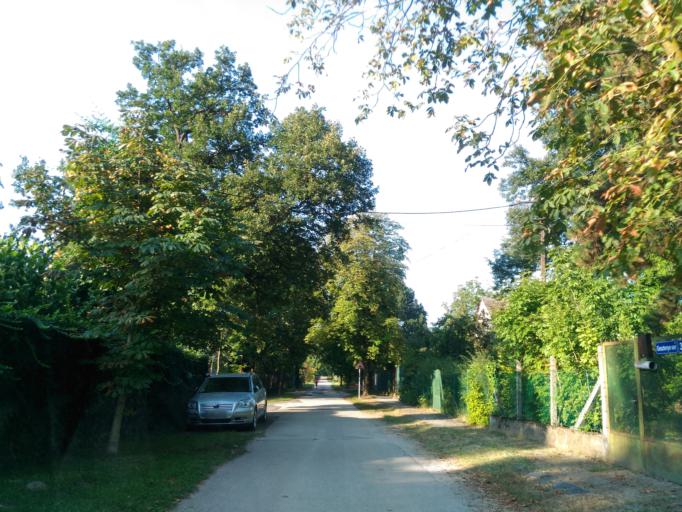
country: HU
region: Veszprem
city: Zanka
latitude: 46.8597
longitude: 17.6668
